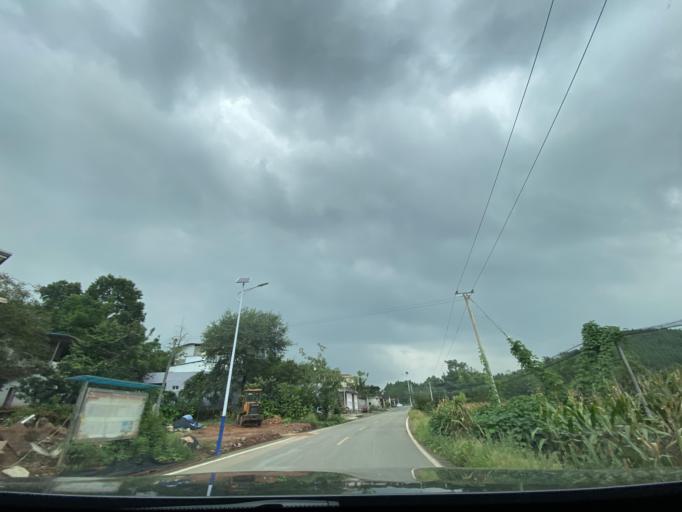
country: CN
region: Sichuan
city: Jiancheng
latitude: 30.5476
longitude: 104.5209
